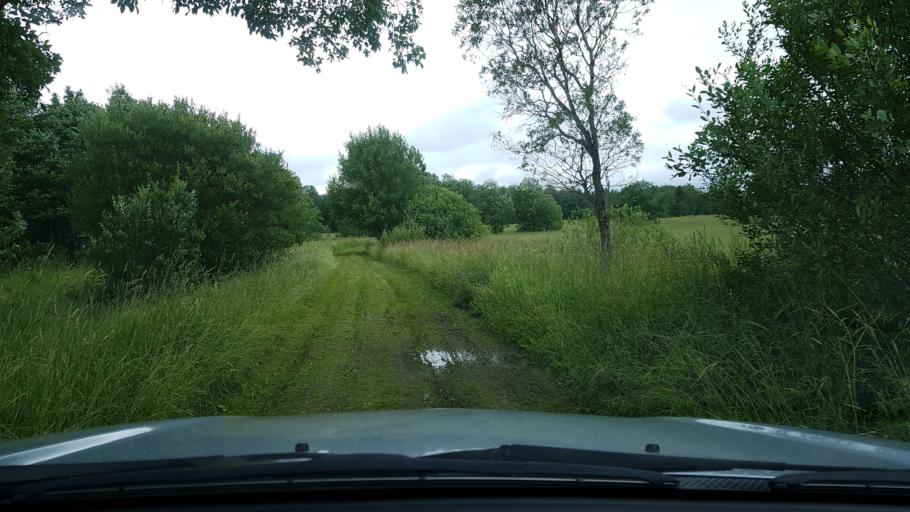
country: EE
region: Ida-Virumaa
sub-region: Narva-Joesuu linn
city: Narva-Joesuu
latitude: 59.3482
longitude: 28.0141
